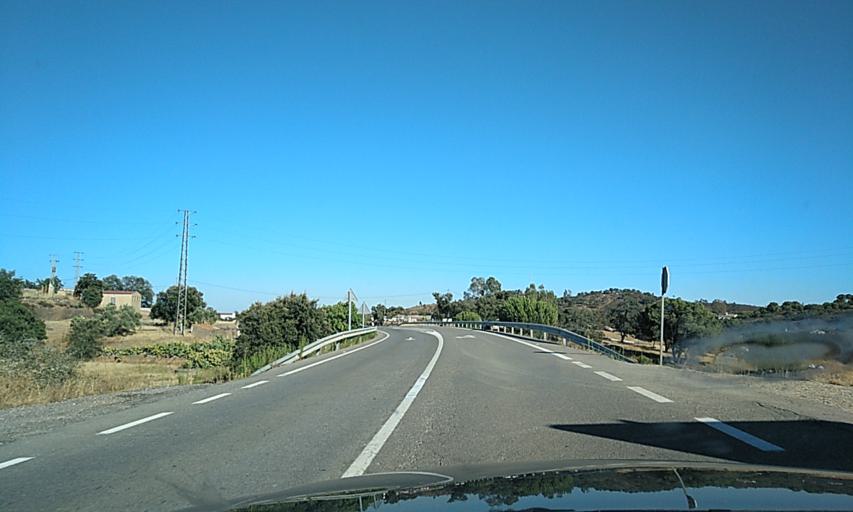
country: ES
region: Andalusia
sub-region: Provincia de Huelva
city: Santa Barbara de Casa
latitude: 37.7948
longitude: -7.1949
